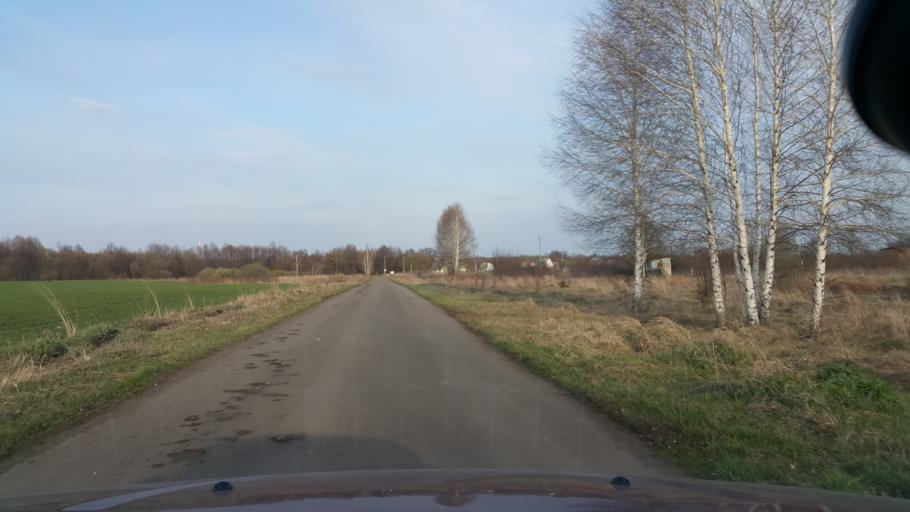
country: RU
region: Tambov
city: Kotovsk
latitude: 52.5900
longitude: 41.4575
